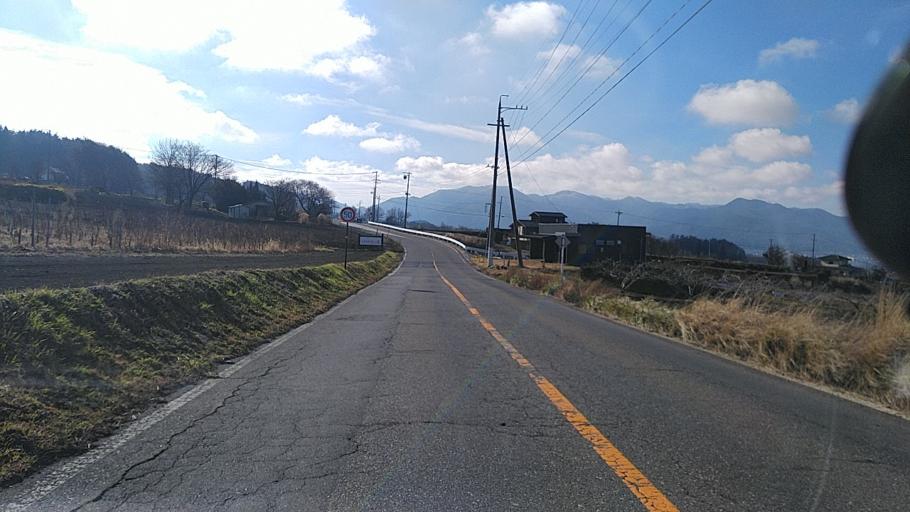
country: JP
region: Nagano
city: Shiojiri
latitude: 36.1373
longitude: 137.9882
